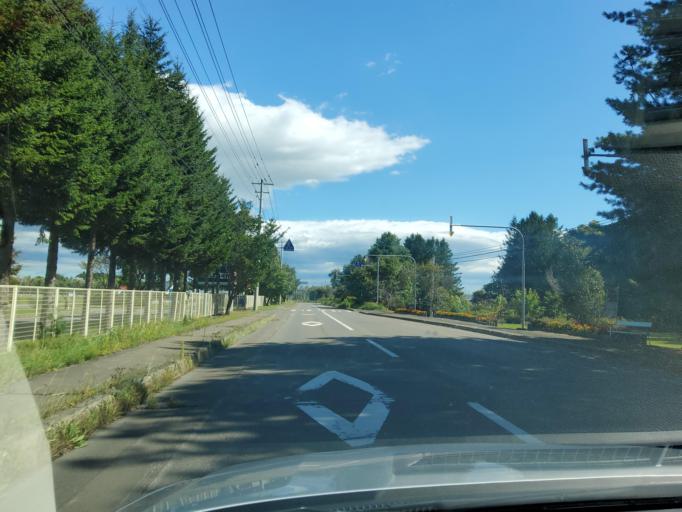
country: JP
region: Hokkaido
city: Obihiro
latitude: 42.9371
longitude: 143.2884
